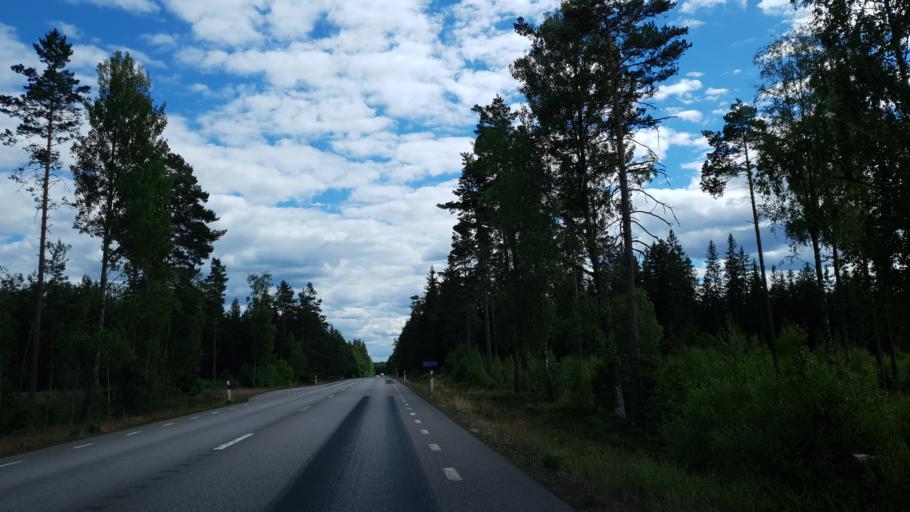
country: SE
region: Kronoberg
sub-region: Uppvidinge Kommun
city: Lenhovda
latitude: 56.8900
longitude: 15.3730
